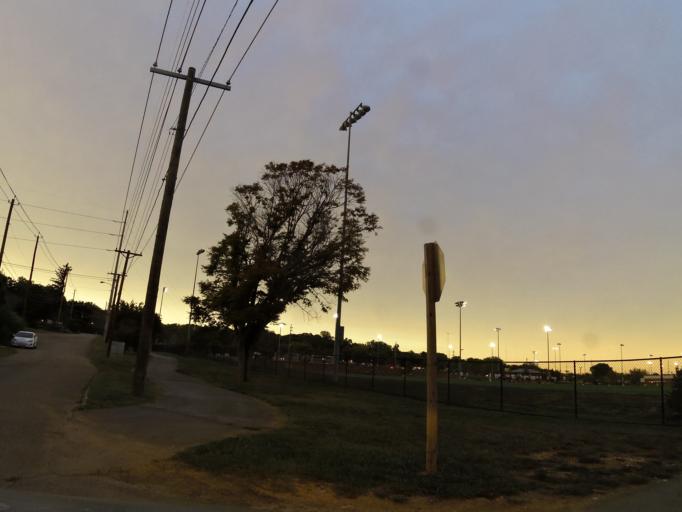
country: US
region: Tennessee
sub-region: Knox County
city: Knoxville
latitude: 35.9428
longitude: -83.9808
